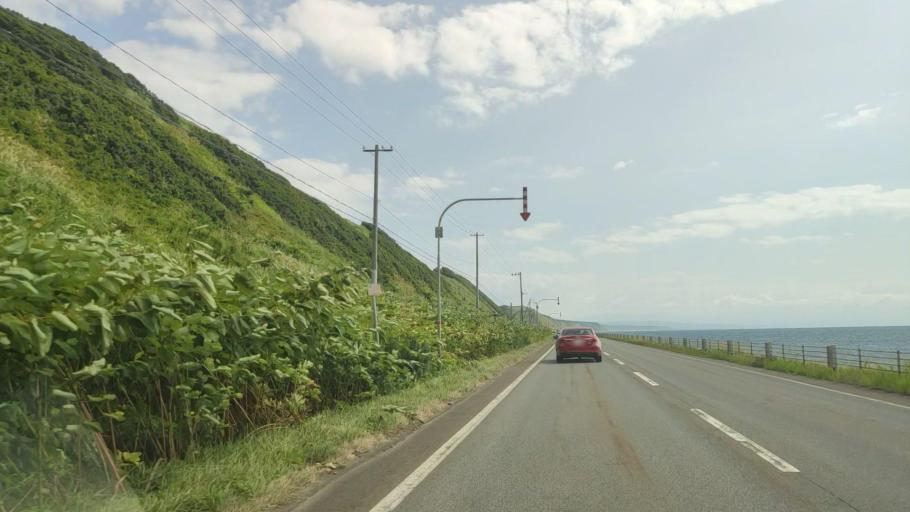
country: JP
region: Hokkaido
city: Rumoi
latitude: 44.0823
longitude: 141.6621
